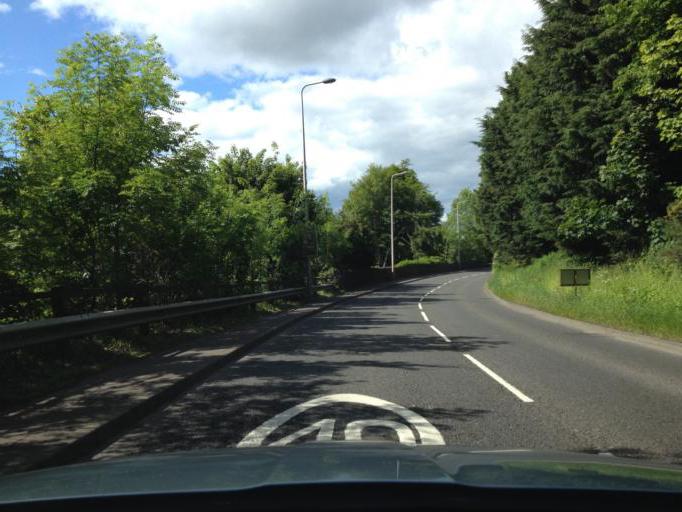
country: GB
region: Scotland
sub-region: Perth and Kinross
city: Perth
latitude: 56.3862
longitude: -3.4196
